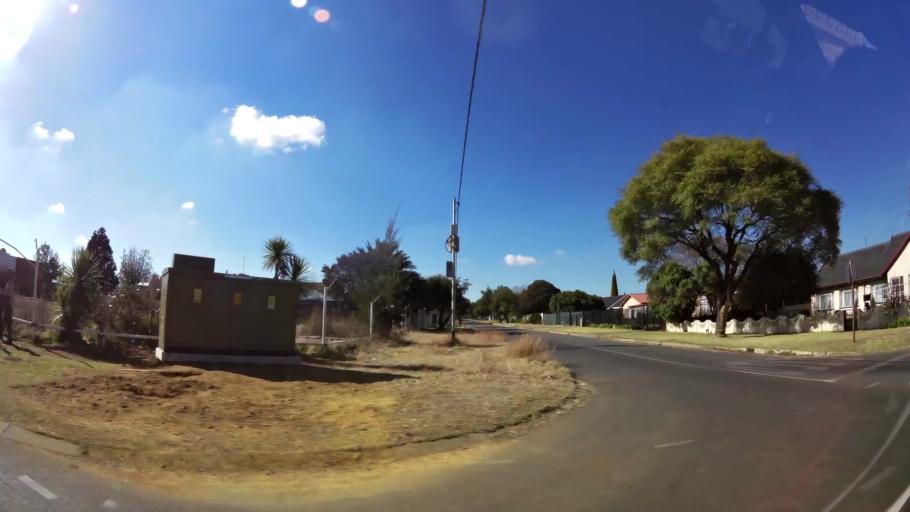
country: ZA
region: Gauteng
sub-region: City of Johannesburg Metropolitan Municipality
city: Roodepoort
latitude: -26.1350
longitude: 27.8344
